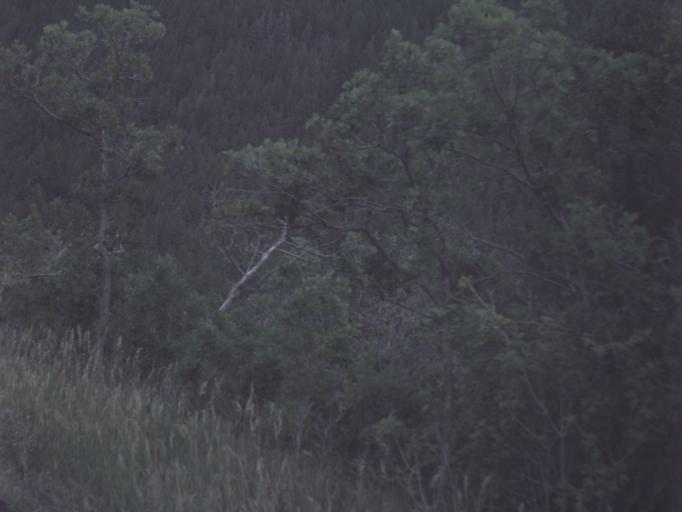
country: US
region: Utah
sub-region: Utah County
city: Cedar Hills
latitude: 40.4493
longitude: -111.6436
